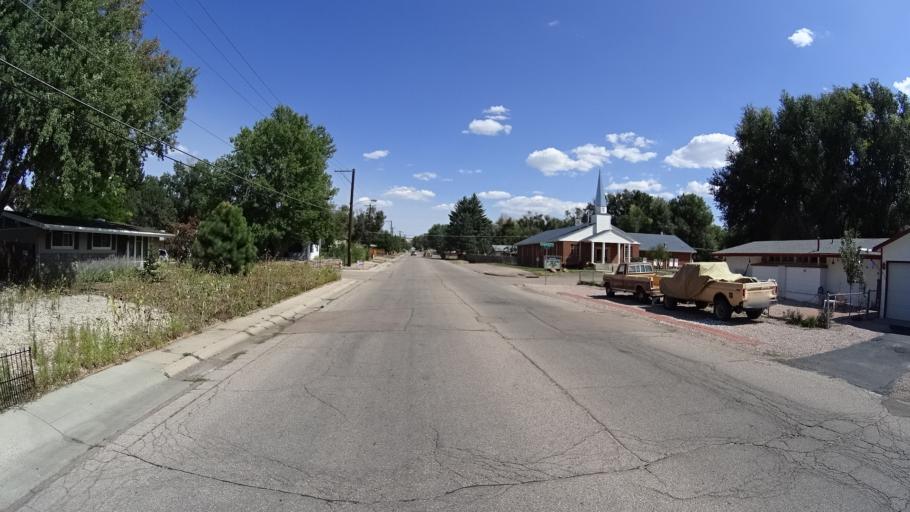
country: US
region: Colorado
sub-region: El Paso County
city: Colorado Springs
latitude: 38.8787
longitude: -104.8071
